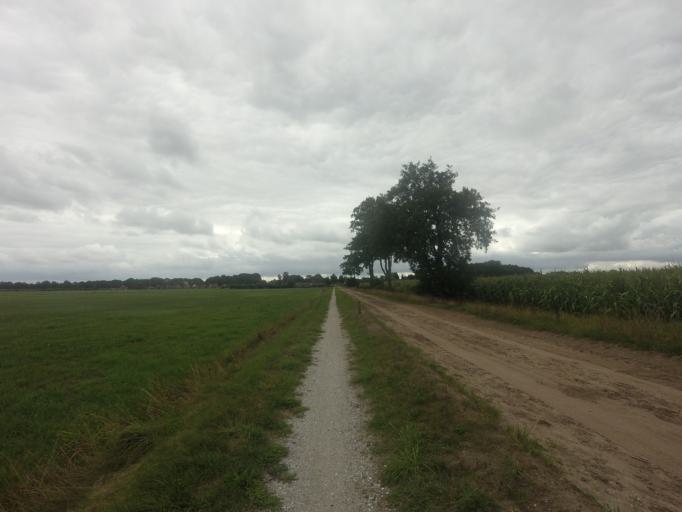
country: NL
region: Friesland
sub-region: Gemeente Weststellingwerf
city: Noordwolde
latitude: 52.9144
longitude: 6.1981
